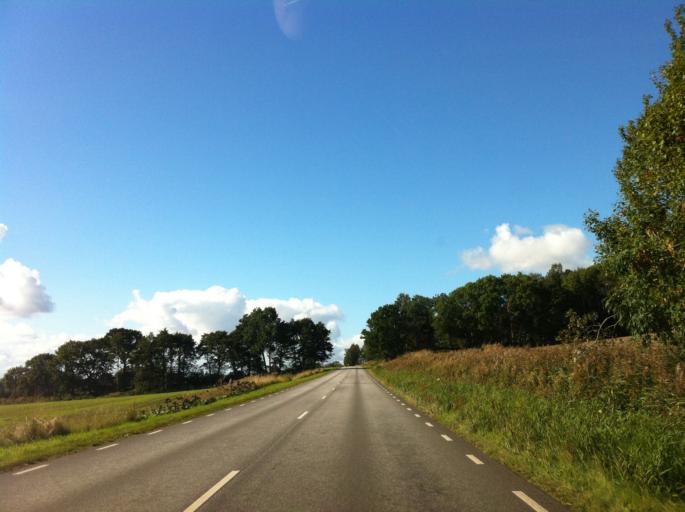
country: SE
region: Skane
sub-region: Hoors Kommun
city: Loberod
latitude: 55.7227
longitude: 13.5084
